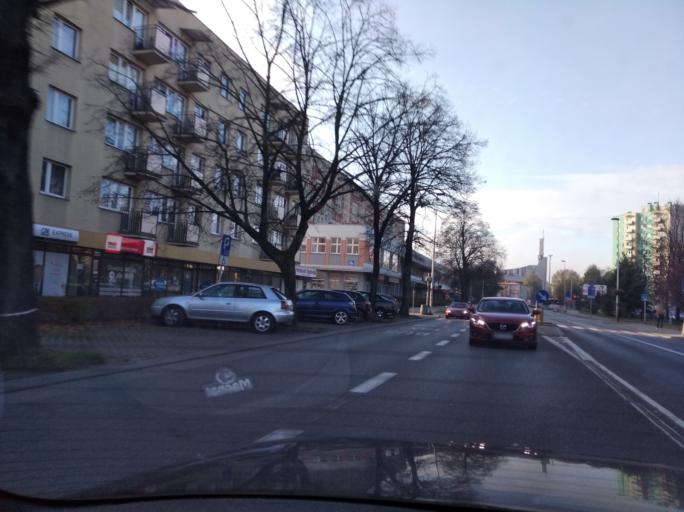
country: PL
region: Subcarpathian Voivodeship
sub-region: Rzeszow
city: Rzeszow
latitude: 50.0274
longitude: 21.9916
